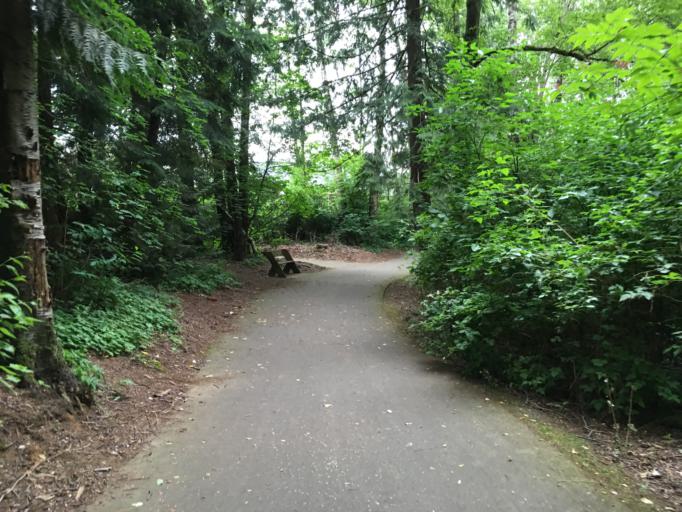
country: US
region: Washington
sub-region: Whatcom County
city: Lynden
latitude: 48.9589
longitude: -122.4227
